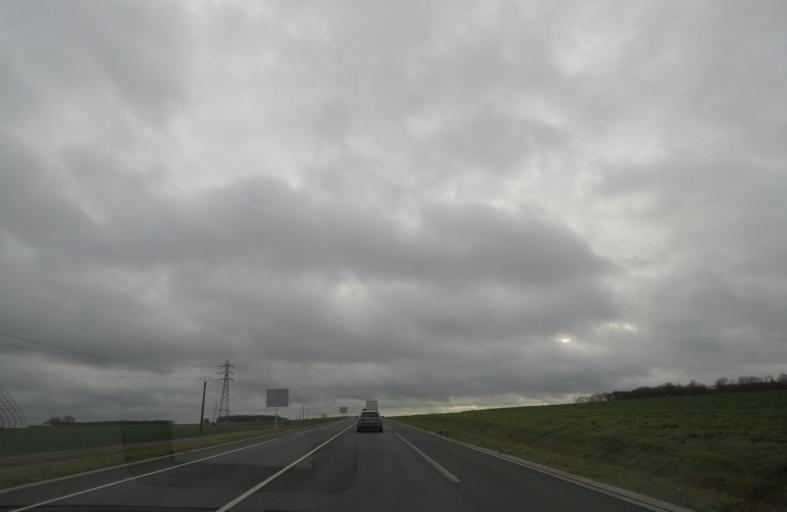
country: FR
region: Centre
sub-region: Departement du Loir-et-Cher
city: Vendome
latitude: 47.7709
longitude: 1.0612
